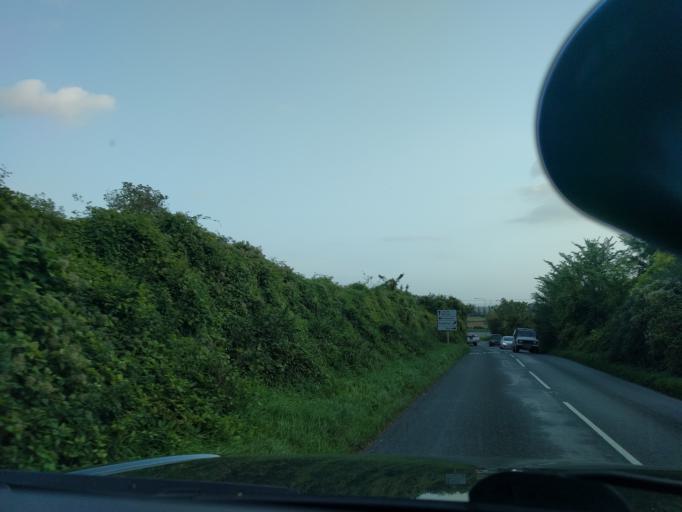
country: GB
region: England
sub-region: Wiltshire
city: Box
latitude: 51.4042
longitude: -2.2330
